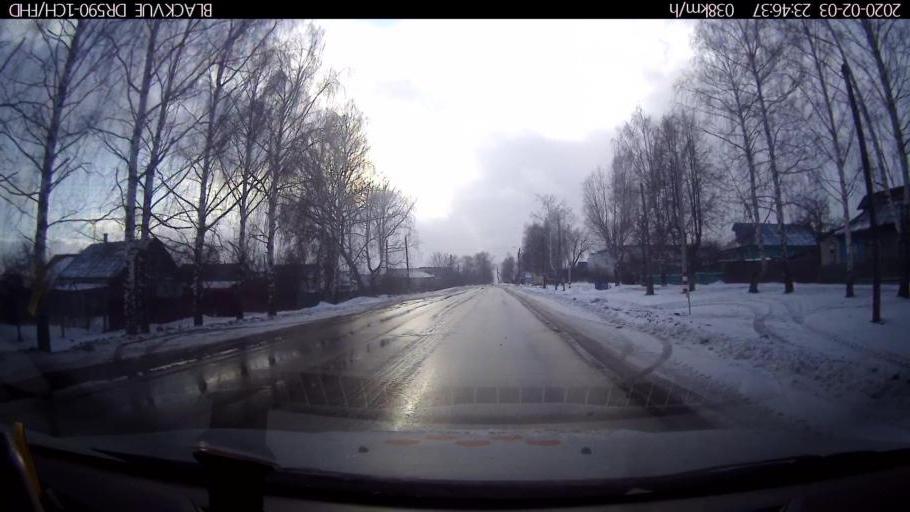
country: RU
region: Nizjnij Novgorod
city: Dal'neye Konstantinovo
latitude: 55.8162
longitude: 44.1041
